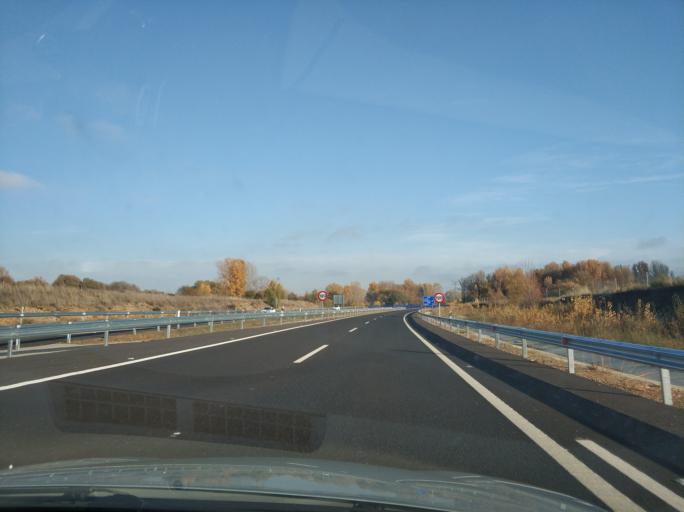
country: ES
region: Castille and Leon
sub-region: Provincia de Leon
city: Mansilla Mayor
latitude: 42.5520
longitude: -5.4543
